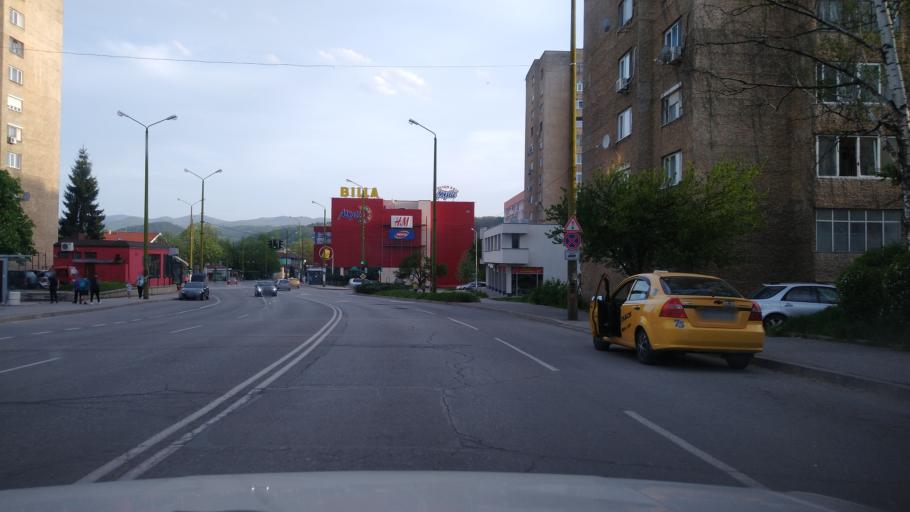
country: BG
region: Gabrovo
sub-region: Obshtina Gabrovo
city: Gabrovo
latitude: 42.8876
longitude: 25.3132
